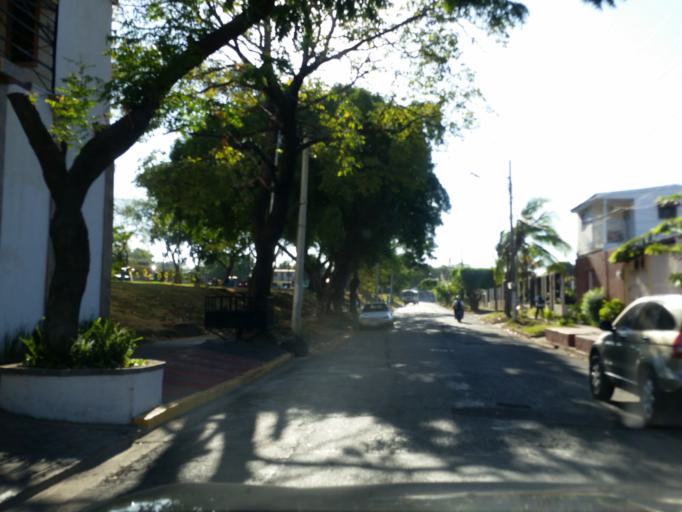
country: NI
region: Managua
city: Managua
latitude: 12.1222
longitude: -86.2703
